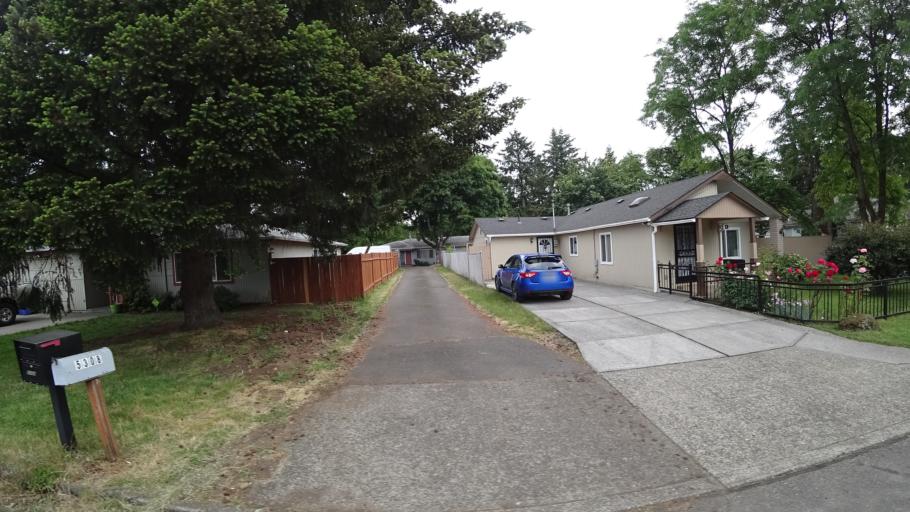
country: US
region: Oregon
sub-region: Multnomah County
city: Lents
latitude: 45.4842
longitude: -122.5419
